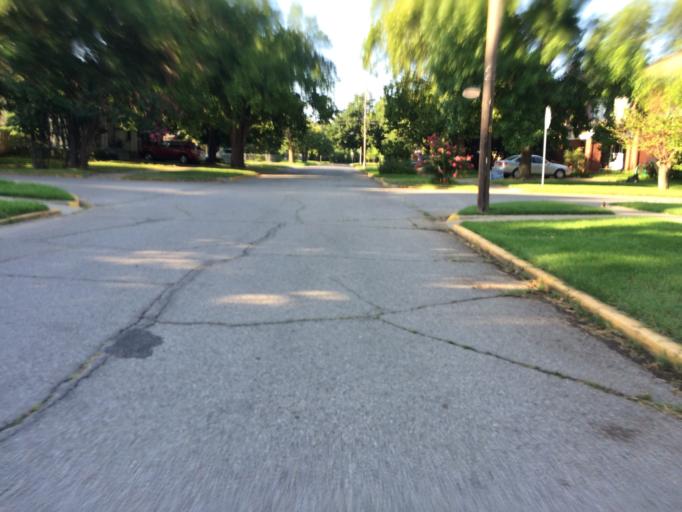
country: US
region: Oklahoma
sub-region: Cleveland County
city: Norman
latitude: 35.2176
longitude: -97.4382
